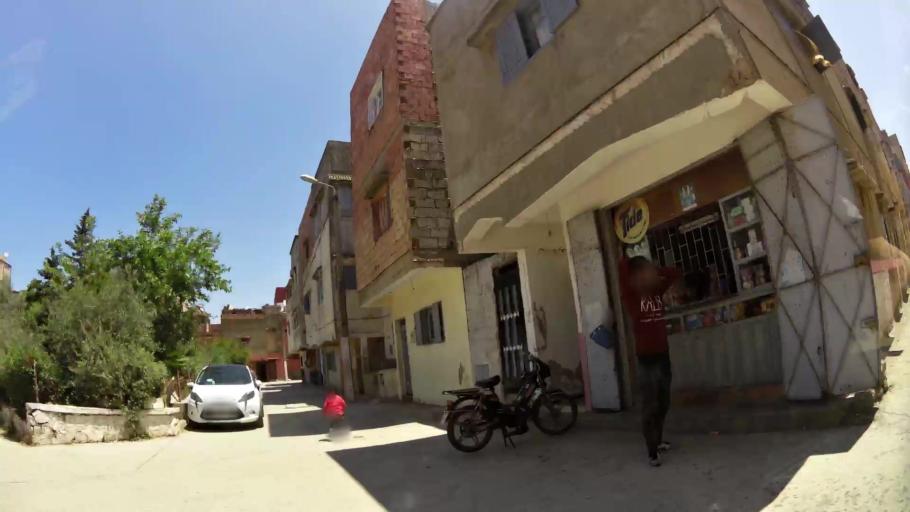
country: MA
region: Rabat-Sale-Zemmour-Zaer
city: Sale
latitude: 34.0705
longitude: -6.7858
